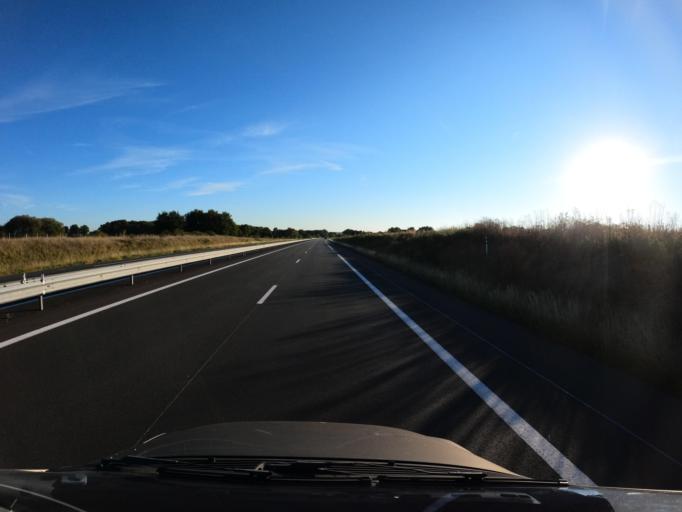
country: FR
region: Pays de la Loire
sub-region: Departement de la Vendee
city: Saint-Fulgent
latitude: 46.8539
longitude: -1.1443
